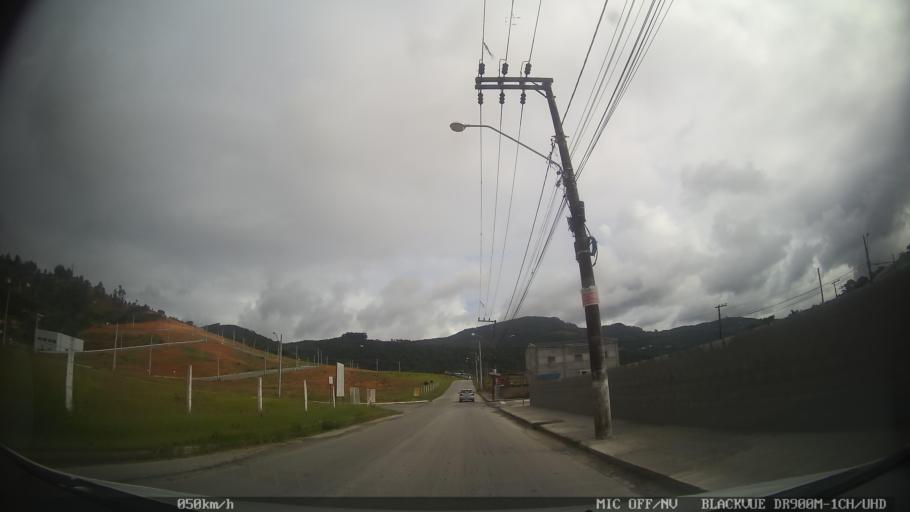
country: BR
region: Santa Catarina
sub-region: Biguacu
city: Biguacu
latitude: -27.5275
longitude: -48.6504
